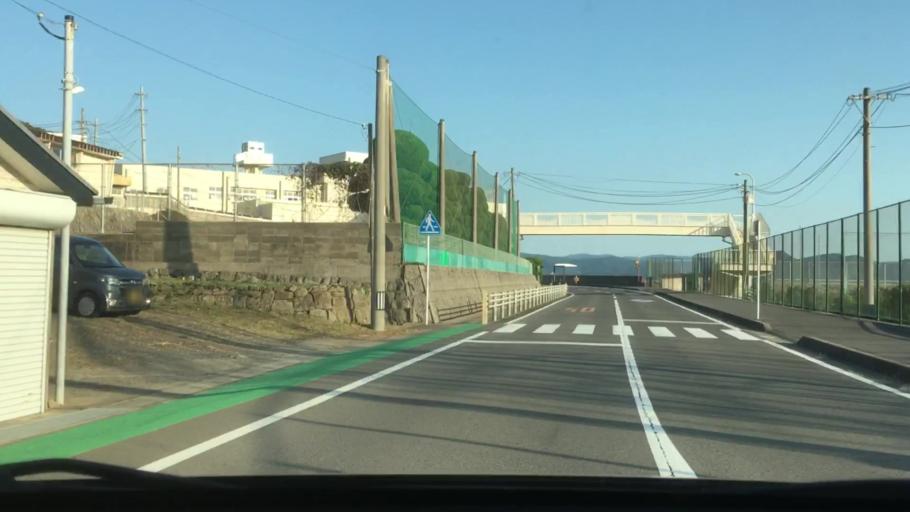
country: JP
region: Nagasaki
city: Sasebo
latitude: 33.0283
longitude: 129.5887
